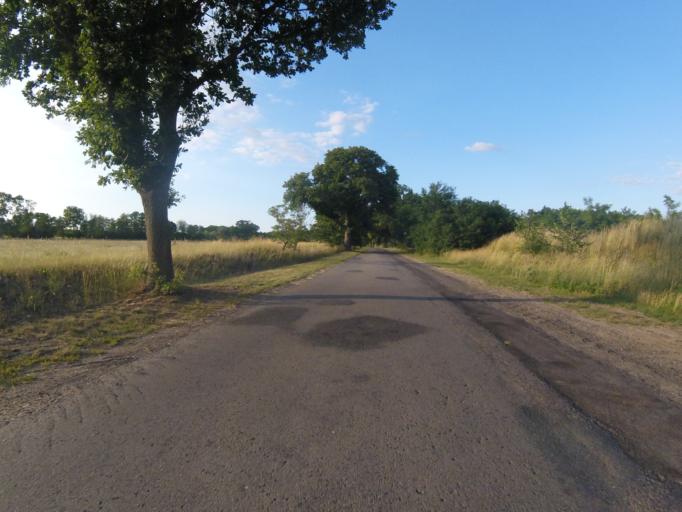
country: DE
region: Brandenburg
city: Mittenwalde
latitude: 52.2401
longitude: 13.5550
